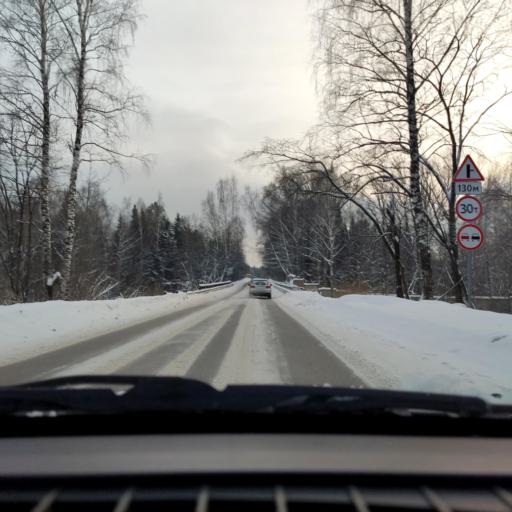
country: RU
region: Perm
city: Overyata
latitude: 58.0513
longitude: 55.8844
